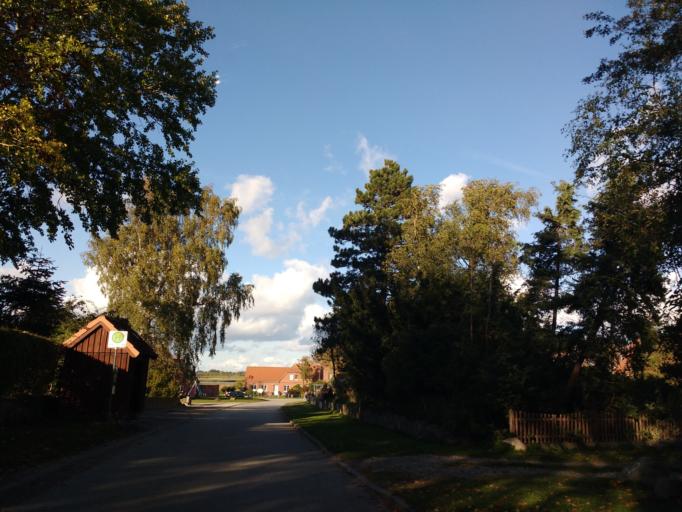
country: DE
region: Schleswig-Holstein
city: Grossenbrode
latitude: 54.4277
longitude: 11.1091
